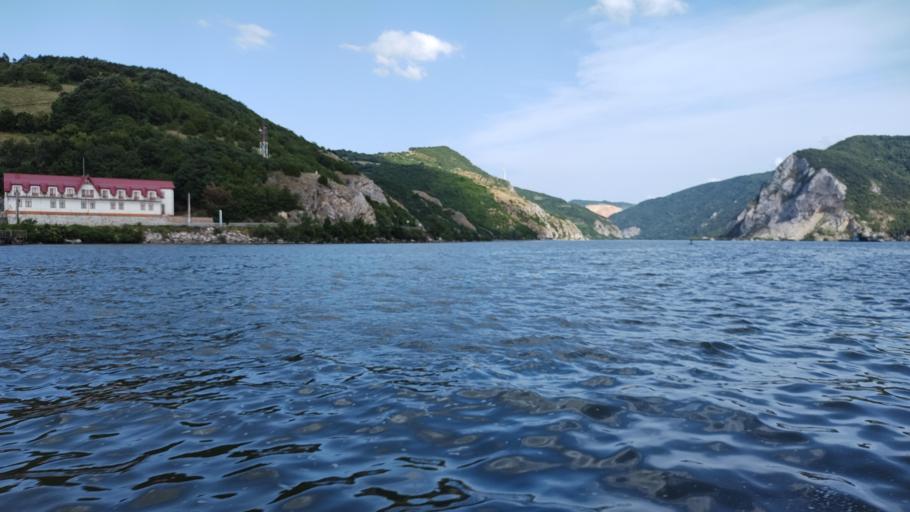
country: RO
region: Caras-Severin
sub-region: Comuna Pescari
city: Coronini
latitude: 44.6711
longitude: 21.6791
